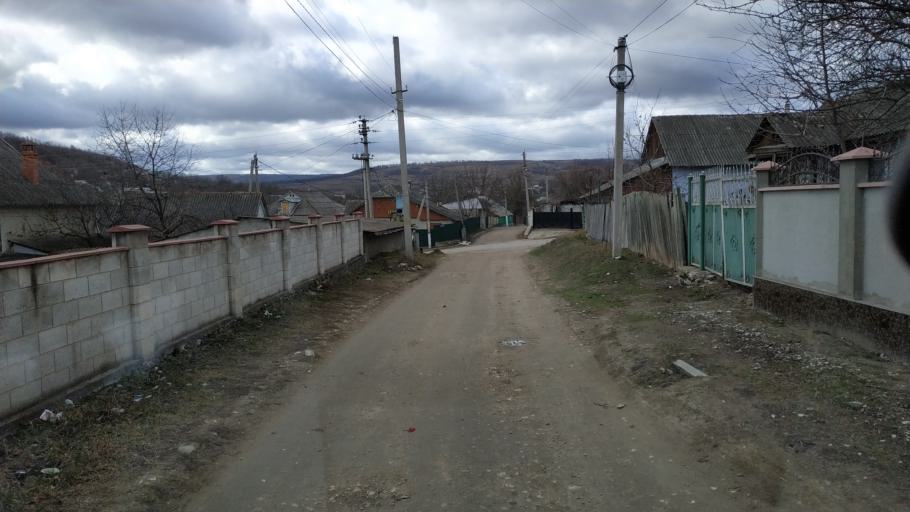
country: MD
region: Stinga Nistrului
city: Bucovat
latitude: 47.1353
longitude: 28.3804
